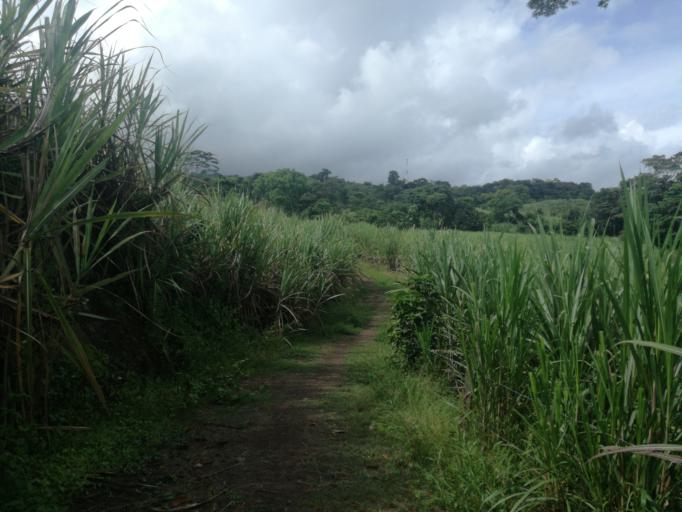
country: CO
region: Boyaca
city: Santana
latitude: 6.0582
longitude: -73.4869
